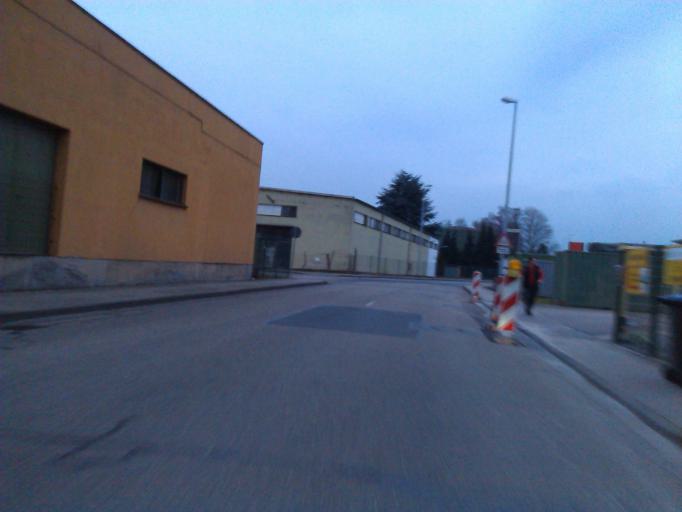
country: DE
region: Rheinland-Pfalz
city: Lahnstein
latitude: 50.3223
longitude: 7.5932
